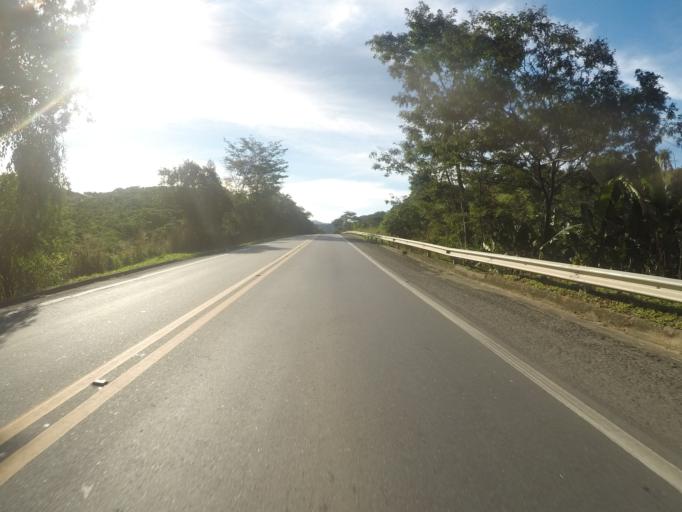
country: BR
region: Espirito Santo
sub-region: Fundao
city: Fundao
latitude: -19.8920
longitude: -40.4127
